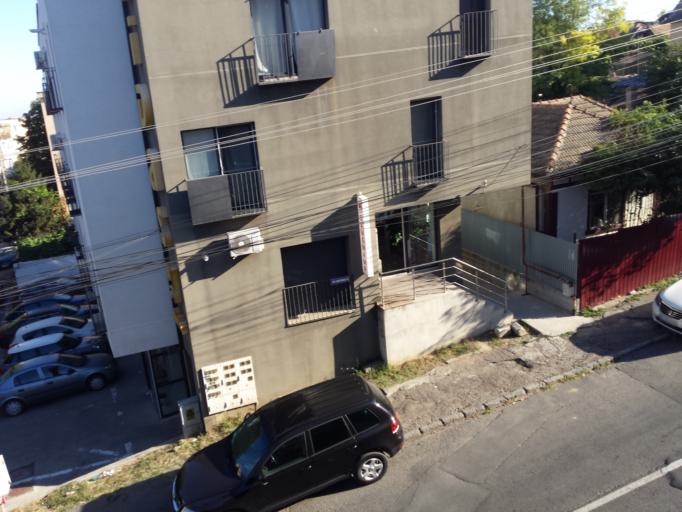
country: RO
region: Tulcea
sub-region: Municipiul Tulcea
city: Tulcea
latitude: 45.1732
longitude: 28.7882
